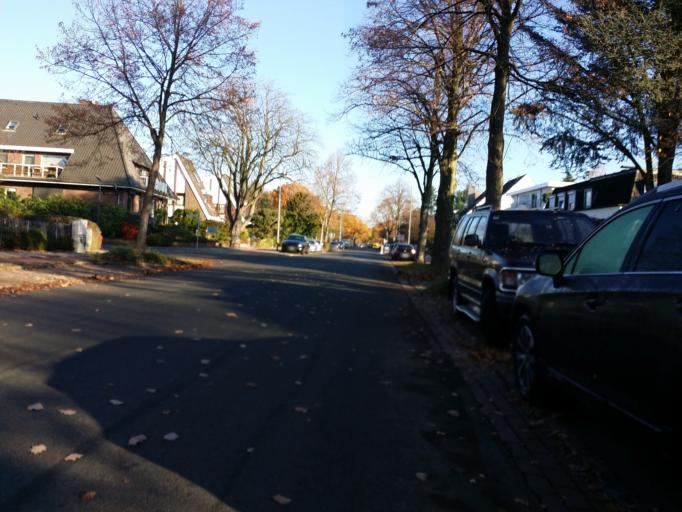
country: DE
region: Bremen
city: Bremen
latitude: 53.0781
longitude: 8.8588
